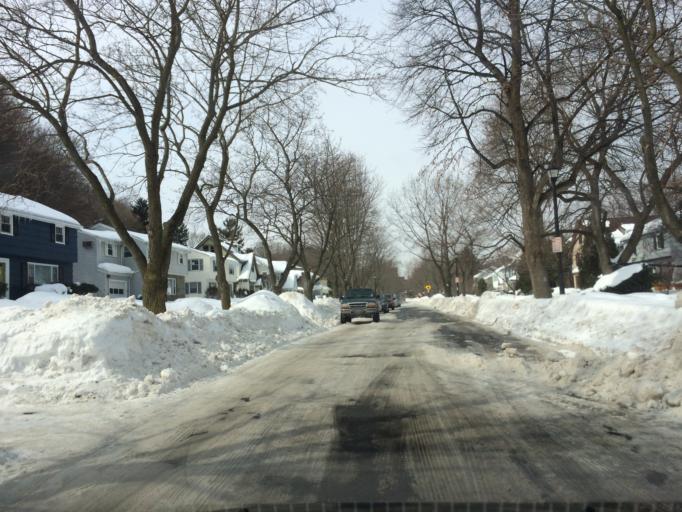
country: US
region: New York
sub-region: Monroe County
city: Rochester
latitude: 43.1336
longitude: -77.5999
